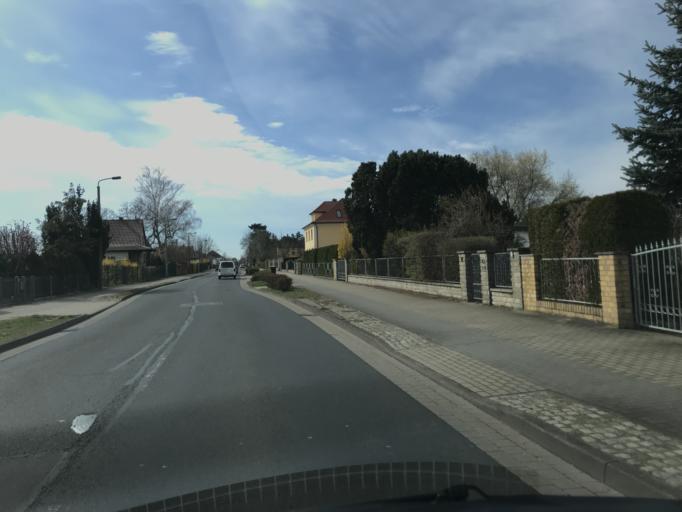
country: DE
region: Saxony
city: Leipzig
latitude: 51.3887
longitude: 12.3264
